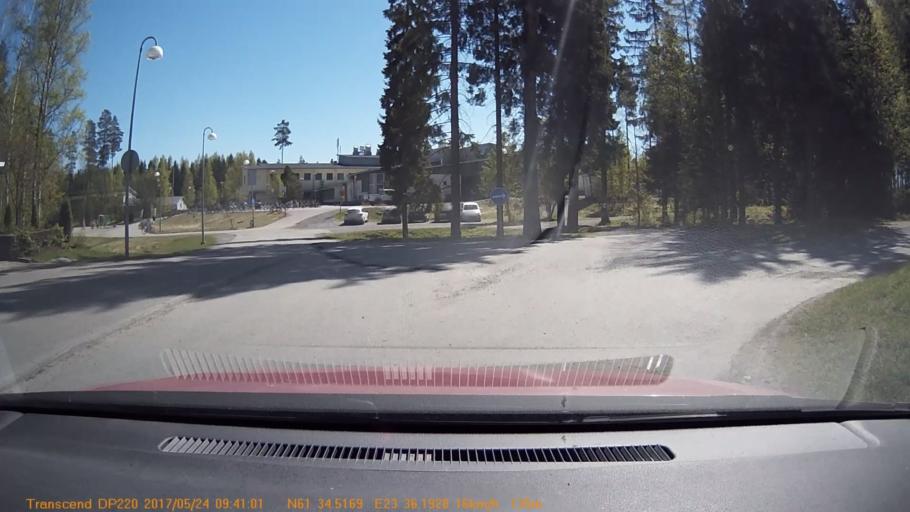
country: FI
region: Pirkanmaa
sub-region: Tampere
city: Yloejaervi
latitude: 61.5753
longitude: 23.6032
